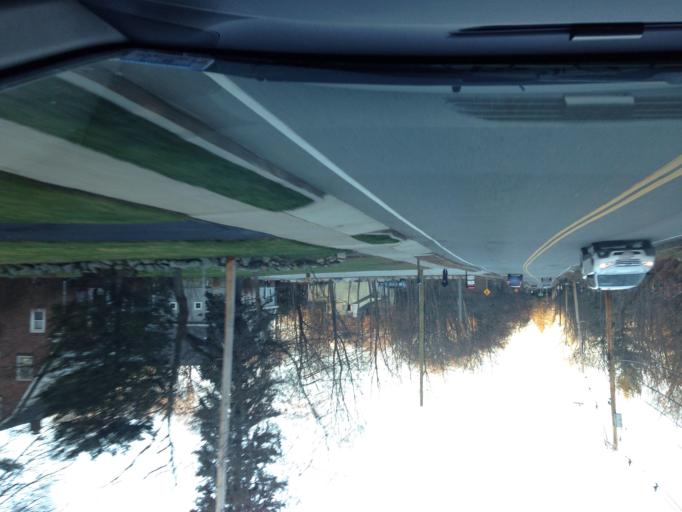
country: US
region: Massachusetts
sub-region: Middlesex County
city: Bedford
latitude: 42.4927
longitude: -71.2889
